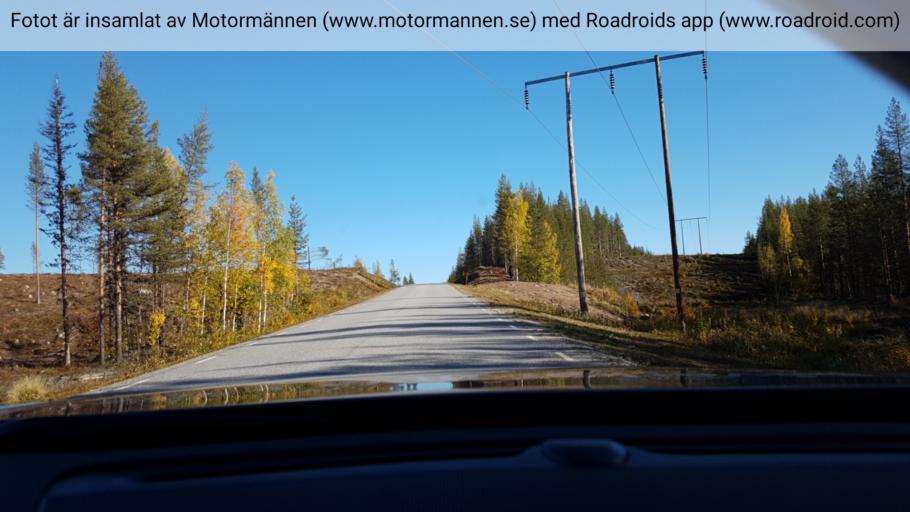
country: SE
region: Norrbotten
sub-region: Gallivare Kommun
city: Gaellivare
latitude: 66.4699
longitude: 20.8431
